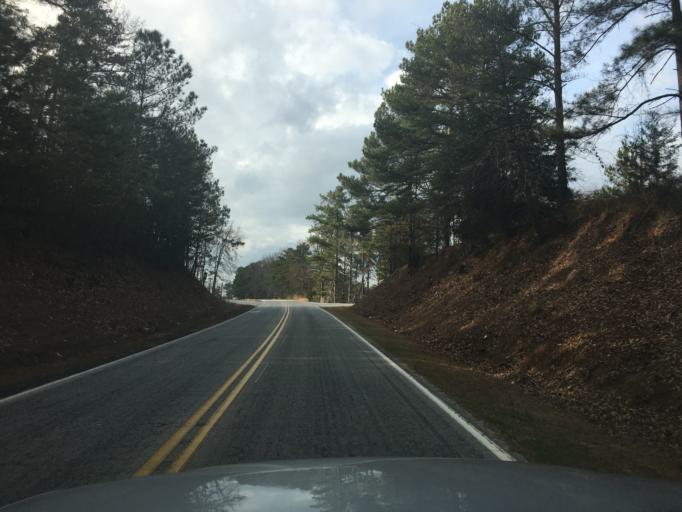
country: US
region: South Carolina
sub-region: Abbeville County
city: Abbeville
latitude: 34.2376
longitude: -82.3963
